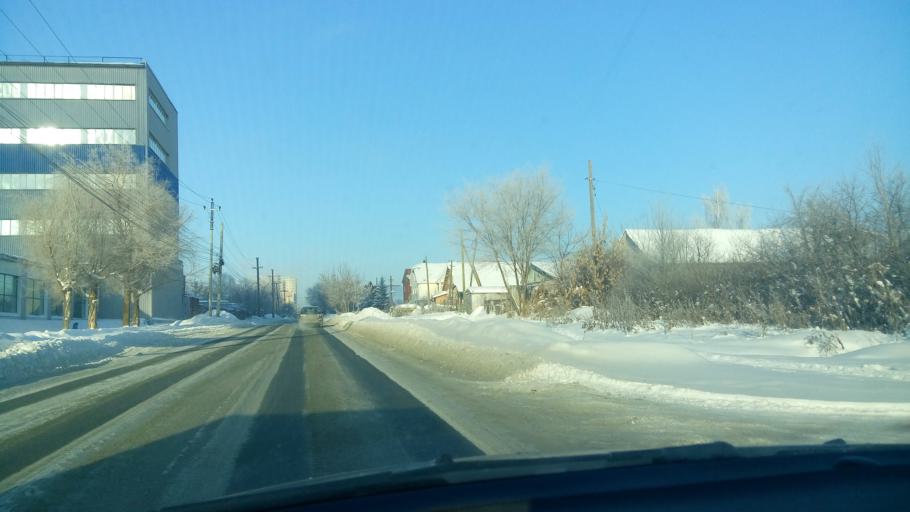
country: RU
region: Chelyabinsk
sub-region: Gorod Chelyabinsk
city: Chelyabinsk
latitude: 55.1275
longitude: 61.3820
